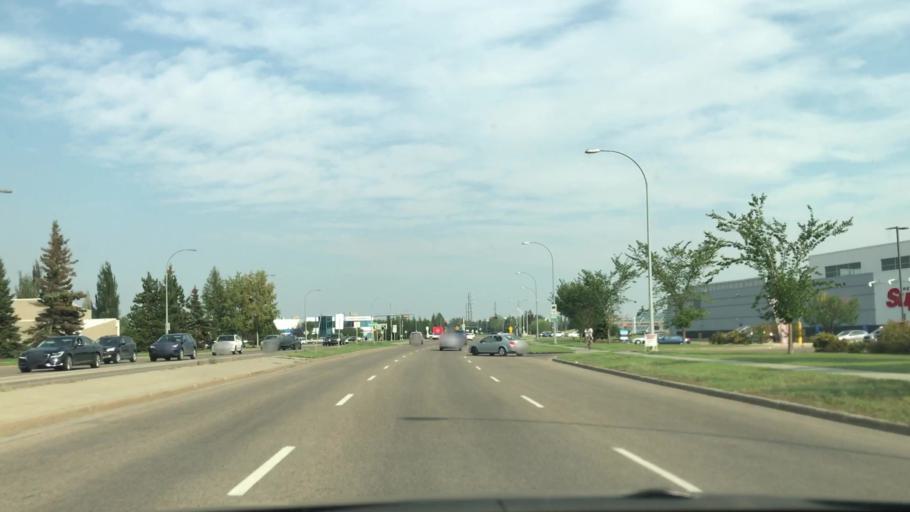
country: CA
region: Alberta
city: Edmonton
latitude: 53.4536
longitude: -113.4827
